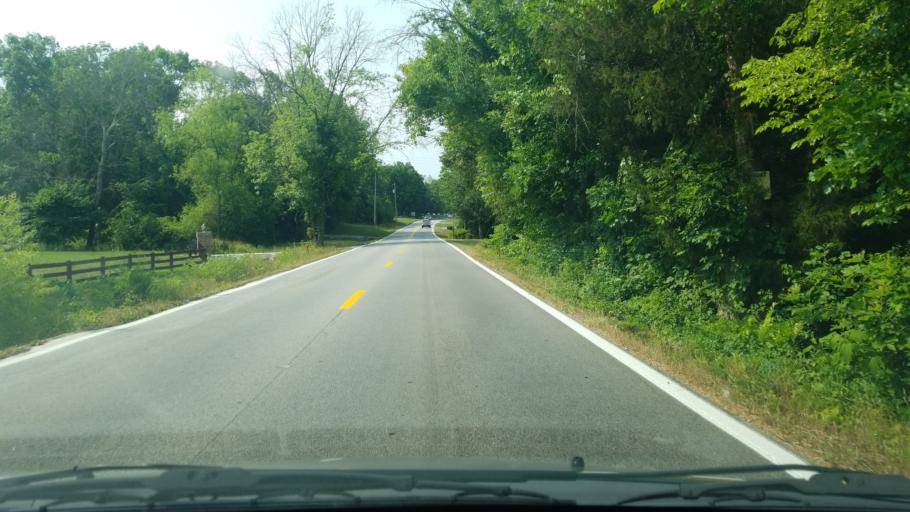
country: US
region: Tennessee
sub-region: Hamilton County
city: East Brainerd
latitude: 34.9891
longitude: -85.0963
